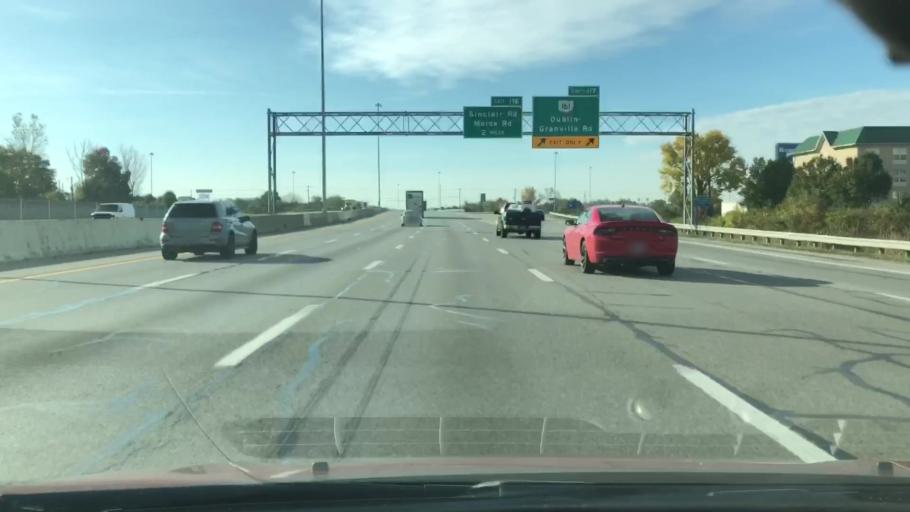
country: US
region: Ohio
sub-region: Franklin County
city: Worthington
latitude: 40.0914
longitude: -82.9872
